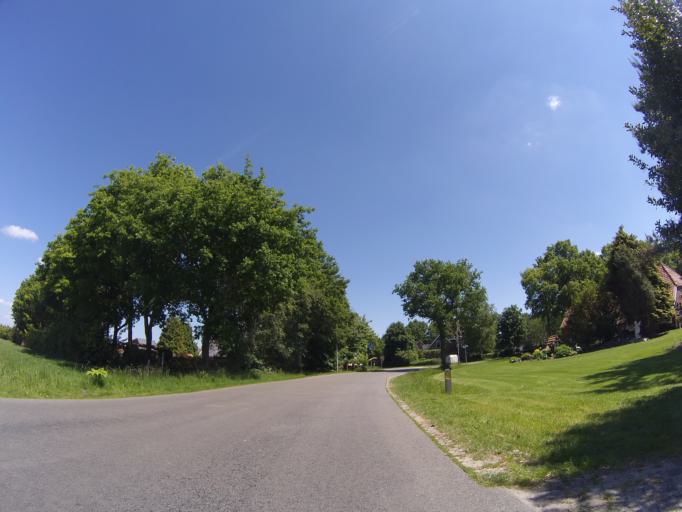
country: NL
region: Drenthe
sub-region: Gemeente Hoogeveen
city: Hoogeveen
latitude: 52.7921
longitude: 6.5418
